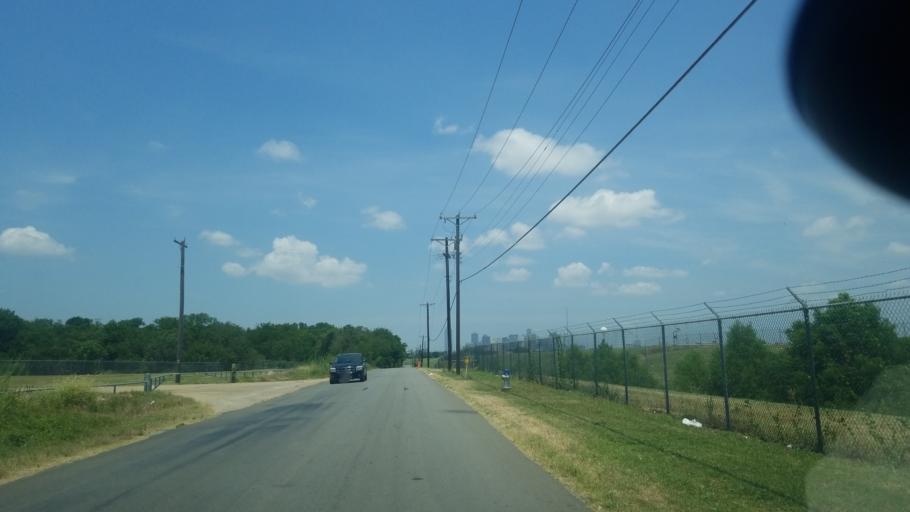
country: US
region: Texas
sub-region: Dallas County
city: Dallas
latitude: 32.7287
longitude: -96.7732
